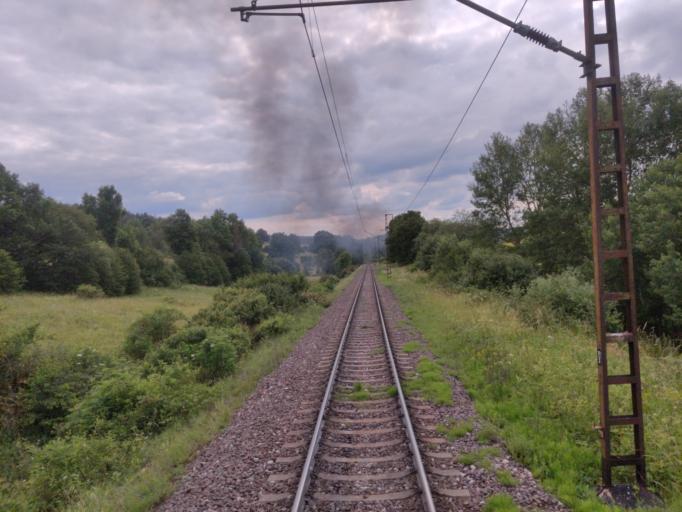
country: DE
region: Saxony-Anhalt
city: Huttenrode
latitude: 51.7654
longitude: 10.8803
